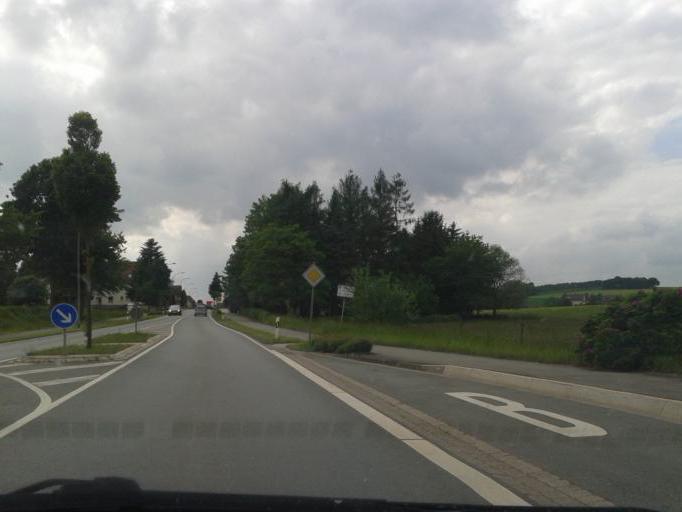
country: DE
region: North Rhine-Westphalia
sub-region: Regierungsbezirk Detmold
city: Steinheim
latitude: 51.8968
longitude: 9.0642
